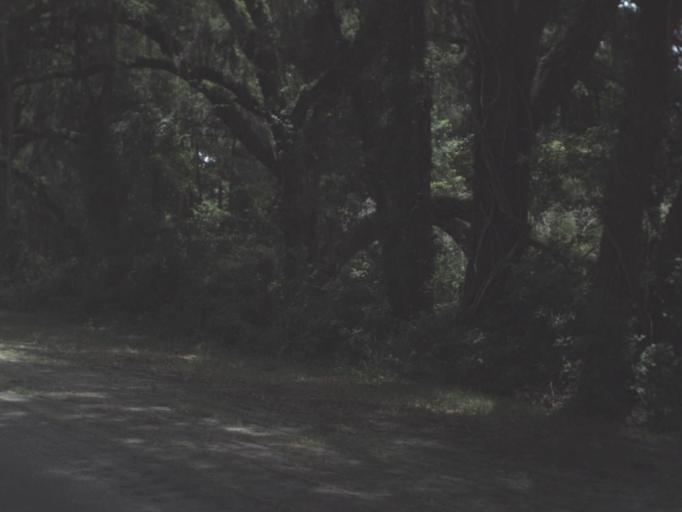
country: US
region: Florida
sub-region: Alachua County
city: Archer
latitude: 29.5444
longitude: -82.3977
